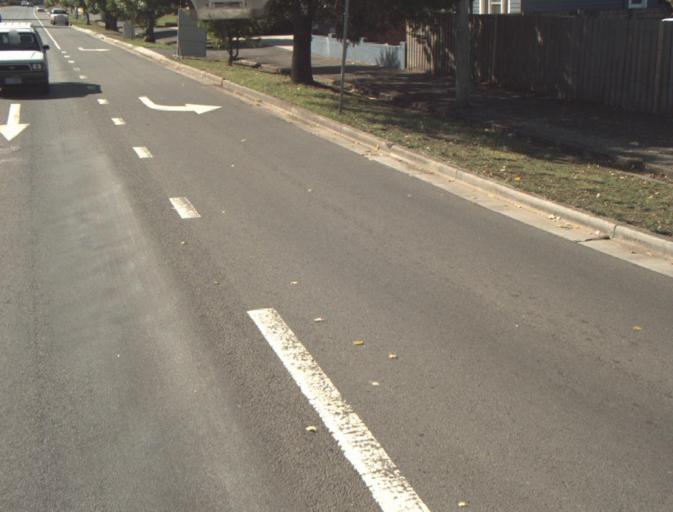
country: AU
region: Tasmania
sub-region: Launceston
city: Launceston
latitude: -41.4252
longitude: 147.1311
